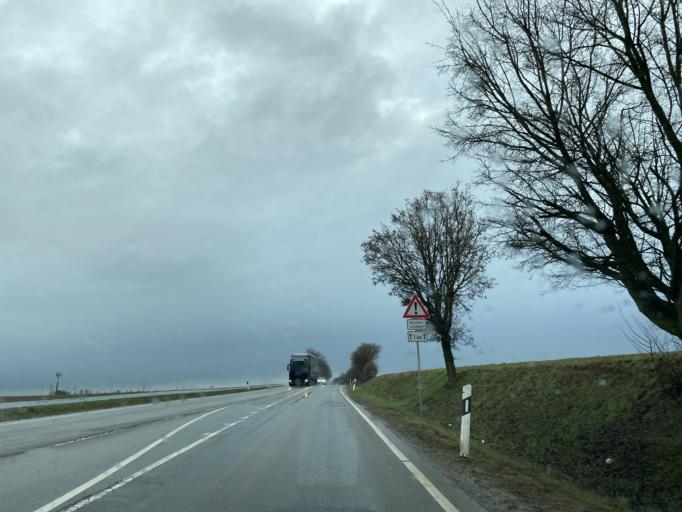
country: DE
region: Baden-Wuerttemberg
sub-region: Regierungsbezirk Stuttgart
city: Hemmingen
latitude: 48.8394
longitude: 9.0210
